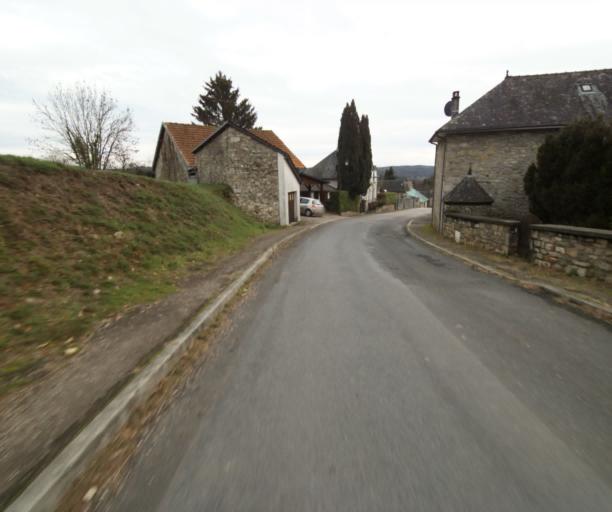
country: FR
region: Limousin
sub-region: Departement de la Correze
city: Chameyrat
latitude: 45.2357
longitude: 1.6973
